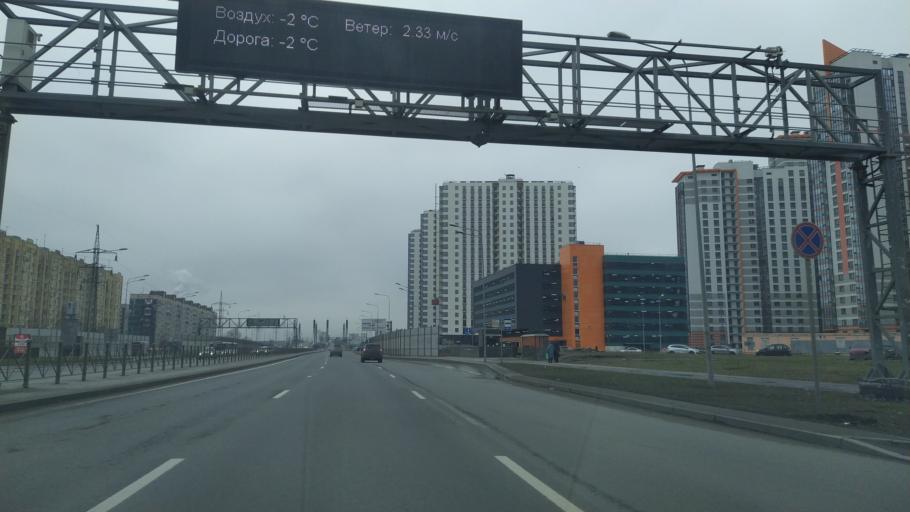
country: RU
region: St.-Petersburg
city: Kupchino
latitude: 59.8307
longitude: 30.3362
